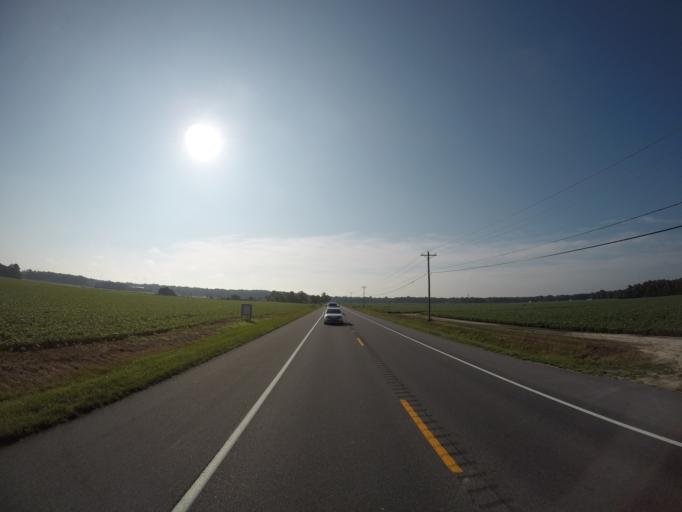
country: US
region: Delaware
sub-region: Sussex County
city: Georgetown
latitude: 38.6963
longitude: -75.4905
